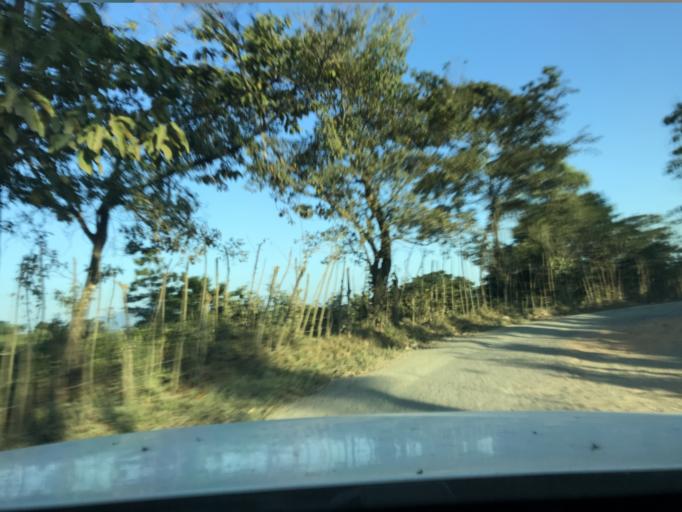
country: GT
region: Izabal
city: Morales
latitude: 15.6403
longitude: -89.0344
